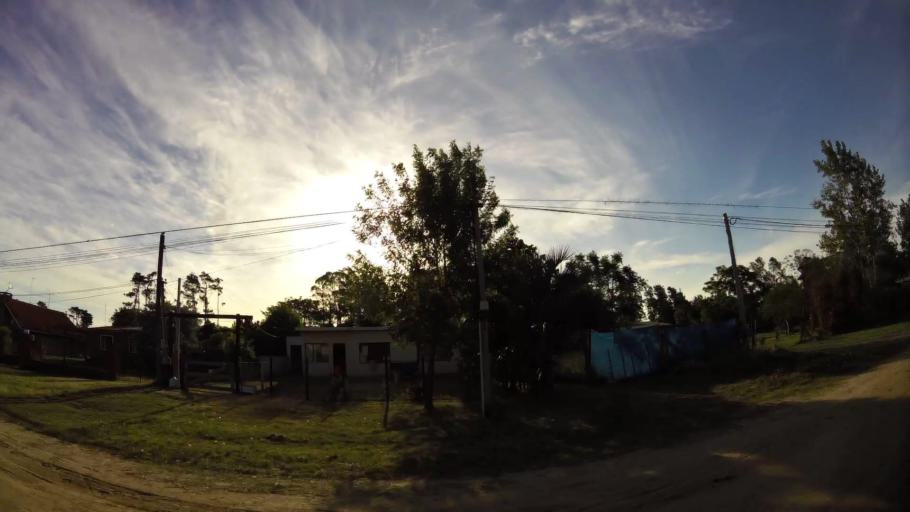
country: UY
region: Canelones
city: Empalme Olmos
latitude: -34.7744
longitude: -55.8567
